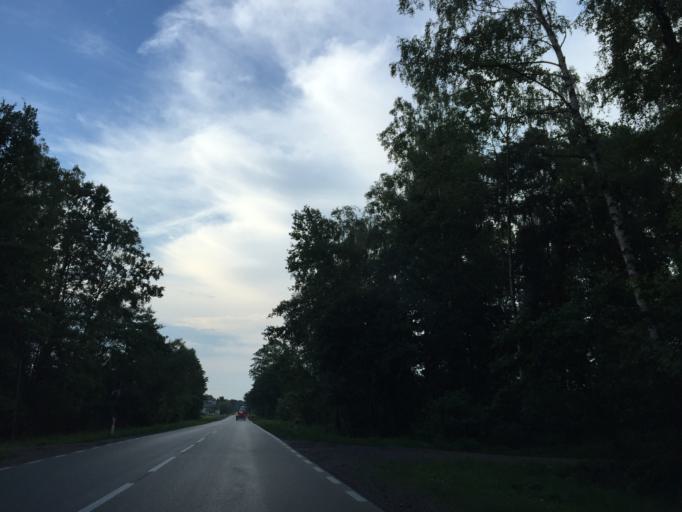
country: PL
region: Masovian Voivodeship
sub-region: Powiat wegrowski
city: Sadowne
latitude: 52.6317
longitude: 21.8446
